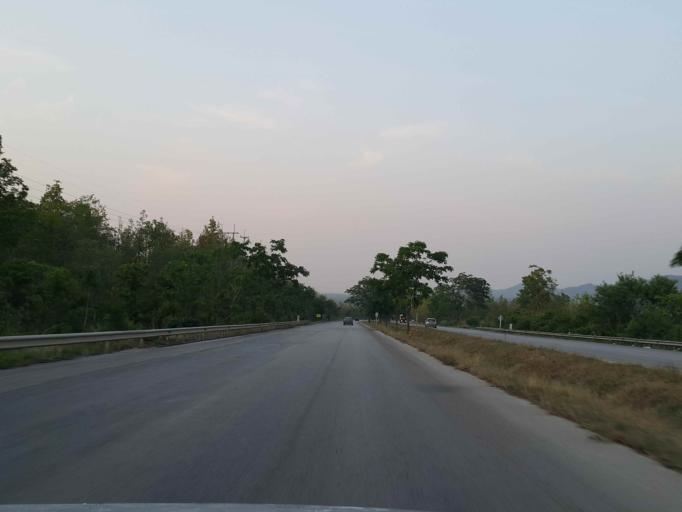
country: TH
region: Lampang
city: Soem Ngam
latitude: 18.0472
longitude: 99.3838
